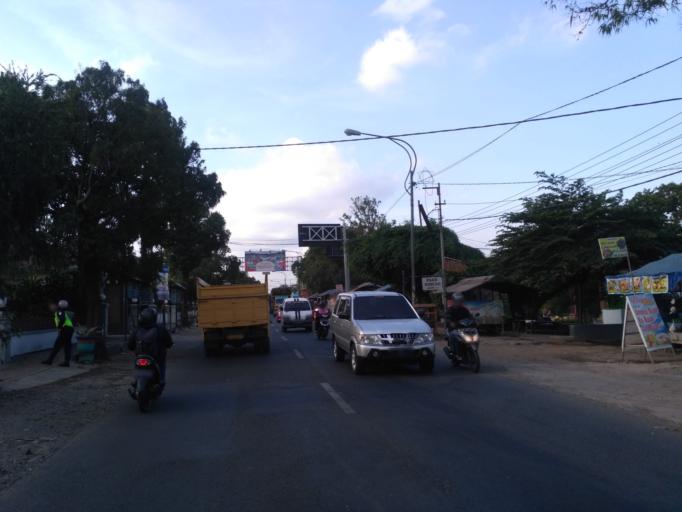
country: ID
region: East Java
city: Kebonsari
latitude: -8.0269
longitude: 112.6161
